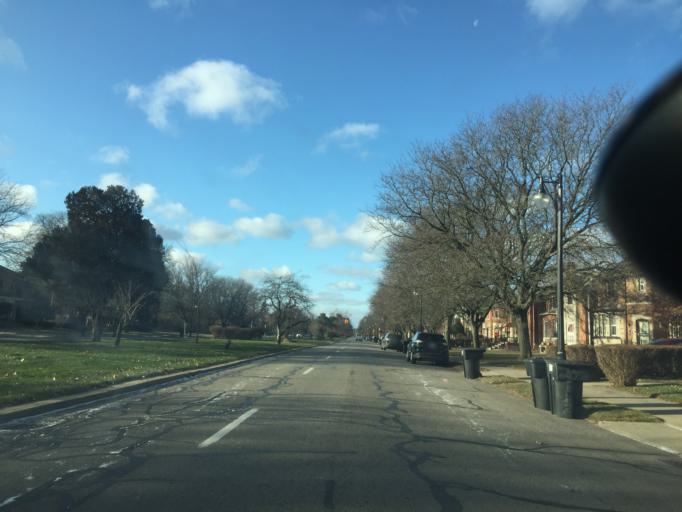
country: US
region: Michigan
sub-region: Wayne County
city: Highland Park
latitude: 42.3932
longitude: -83.1312
